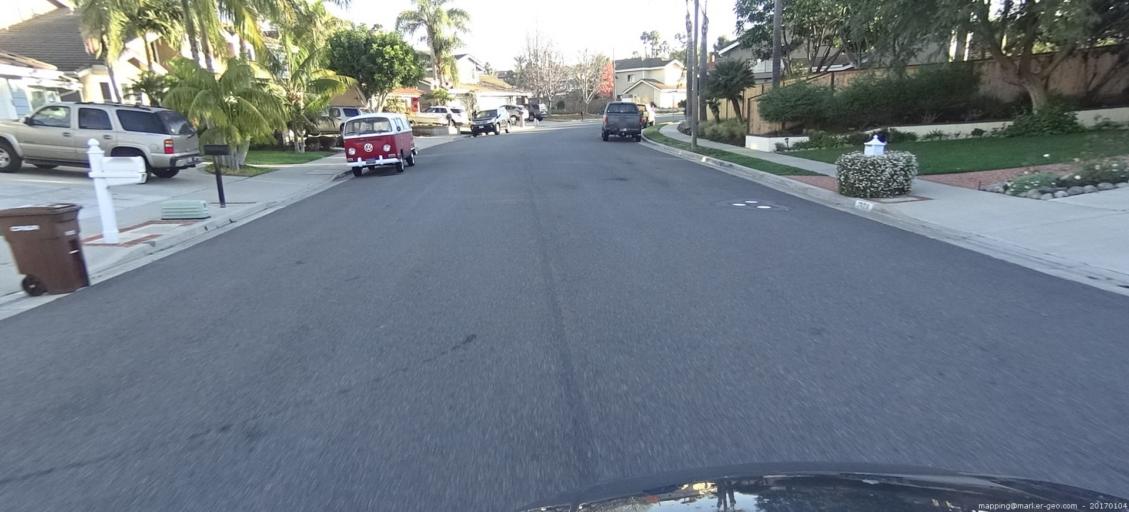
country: US
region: California
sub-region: Orange County
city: Dana Point
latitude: 33.4873
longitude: -117.7056
